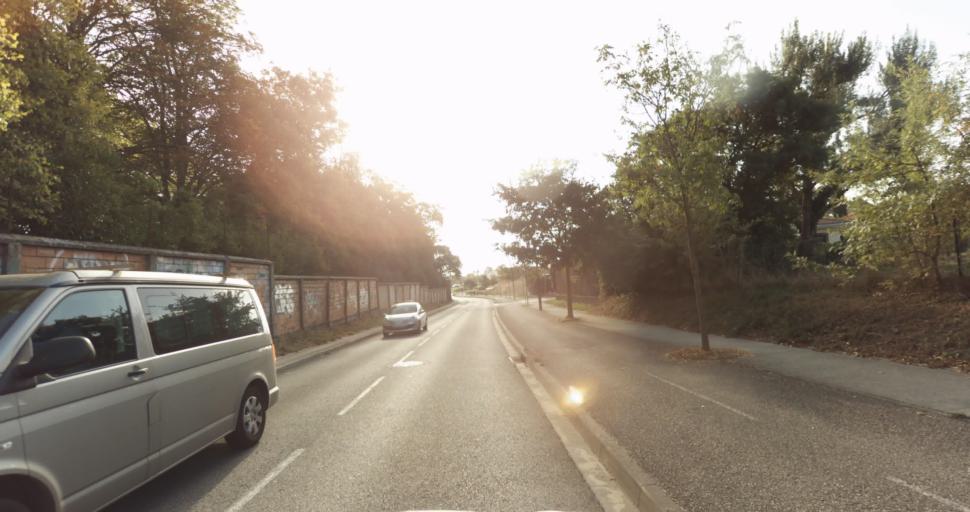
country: FR
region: Midi-Pyrenees
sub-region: Departement de la Haute-Garonne
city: Ramonville-Saint-Agne
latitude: 43.5379
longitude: 1.4666
